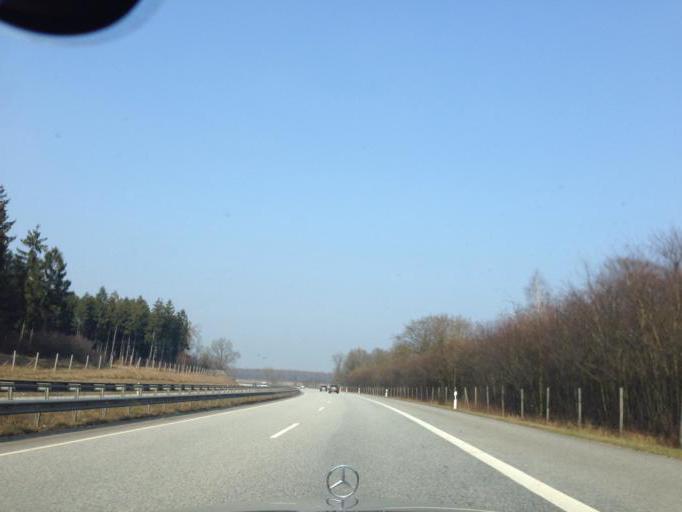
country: DE
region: Schleswig-Holstein
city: Negernbotel
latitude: 53.9970
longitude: 10.2504
